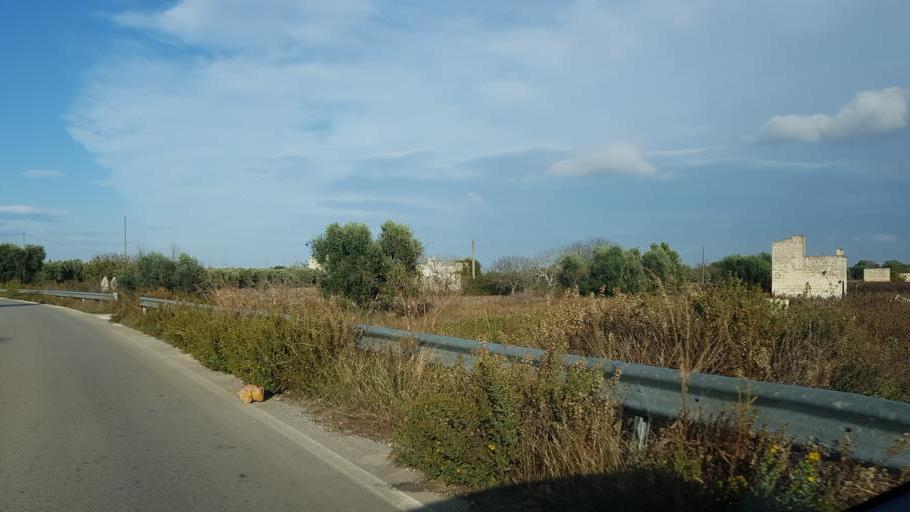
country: IT
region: Apulia
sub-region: Provincia di Brindisi
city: Oria
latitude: 40.5306
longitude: 17.6555
